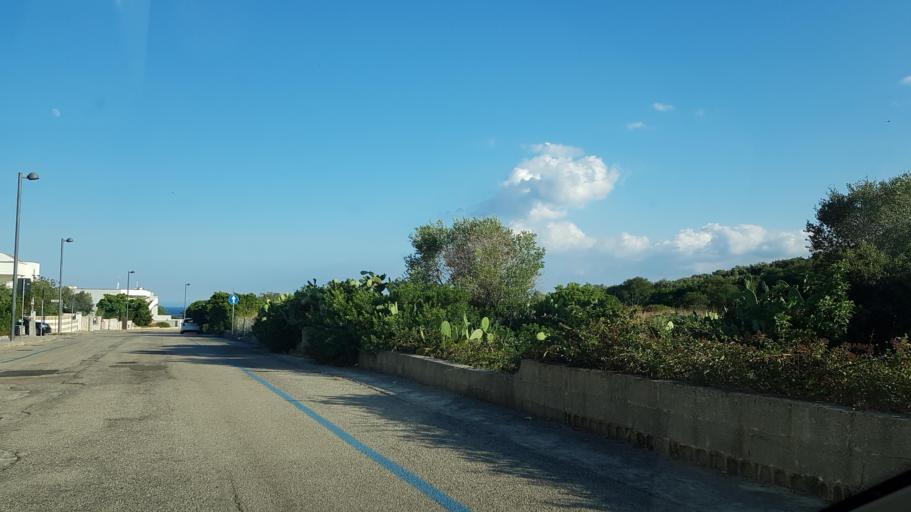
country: IT
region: Apulia
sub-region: Provincia di Lecce
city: Castro
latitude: 40.0050
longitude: 18.4203
